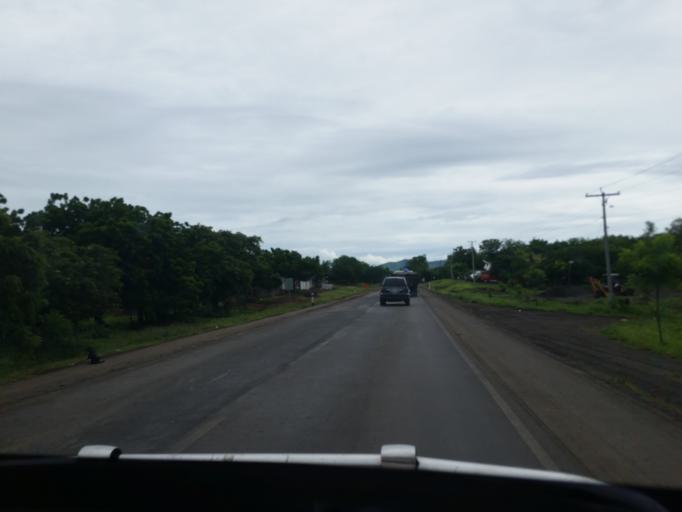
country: NI
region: Managua
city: Tipitapa
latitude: 12.2832
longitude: -86.0621
